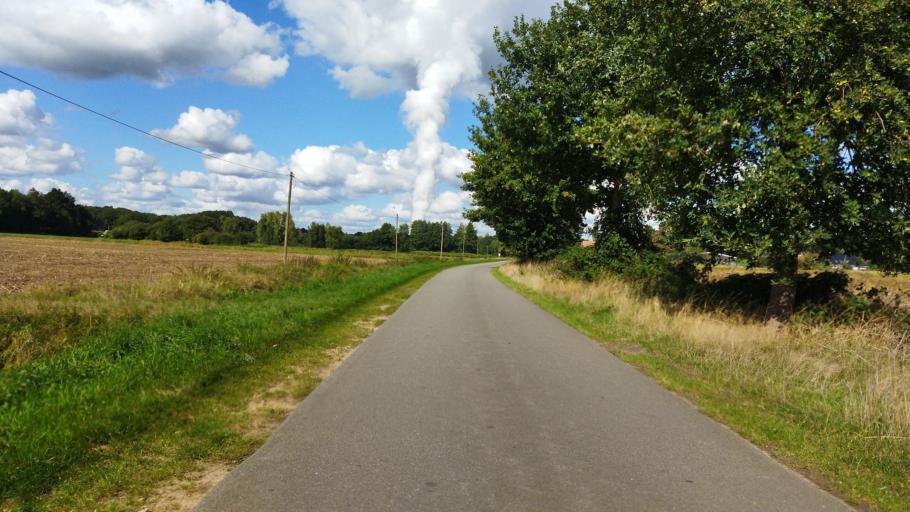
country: DE
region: Lower Saxony
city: Emsburen
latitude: 52.4432
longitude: 7.3388
